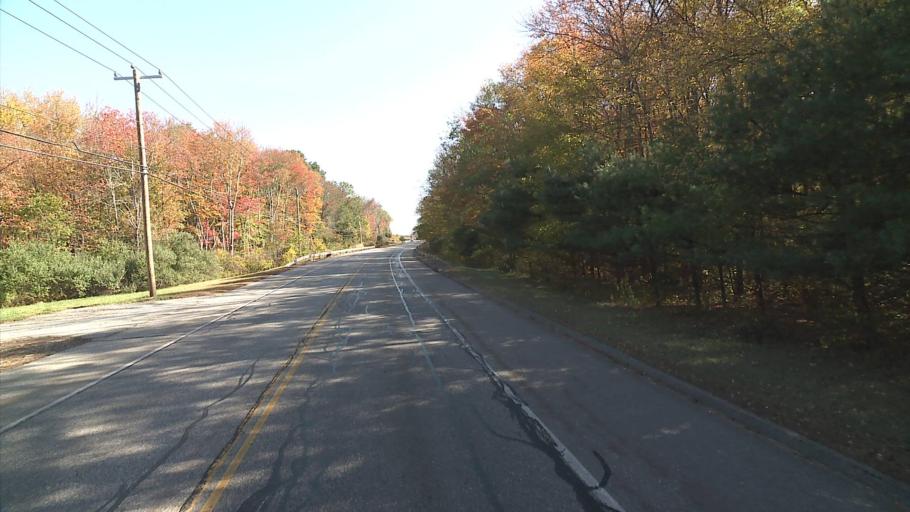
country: US
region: Connecticut
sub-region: Windham County
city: Windham
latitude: 41.7679
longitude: -72.0993
